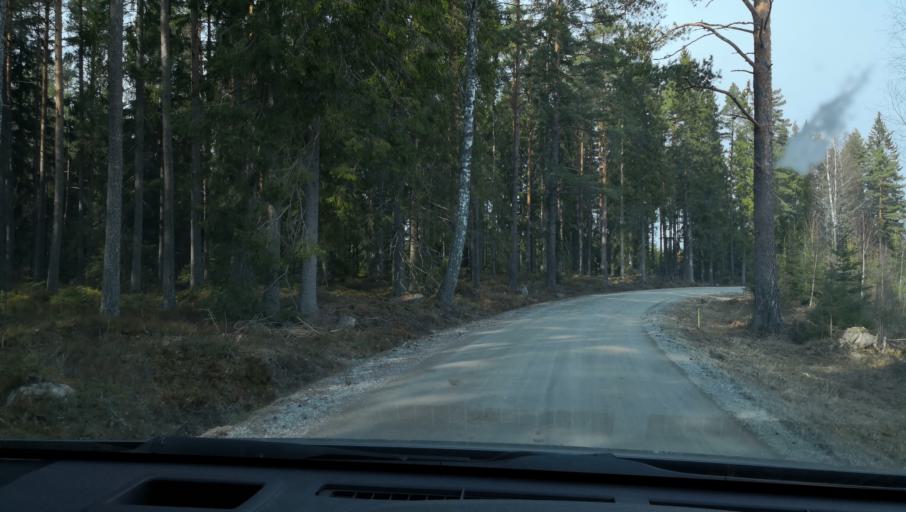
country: SE
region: OErebro
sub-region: Lindesbergs Kommun
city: Frovi
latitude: 59.3609
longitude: 15.4325
